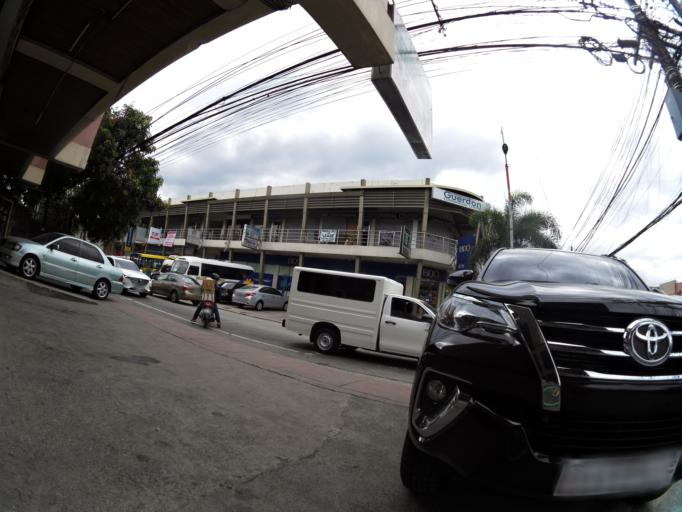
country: PH
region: Calabarzon
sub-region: Province of Rizal
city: Antipolo
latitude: 14.6422
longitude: 121.1107
